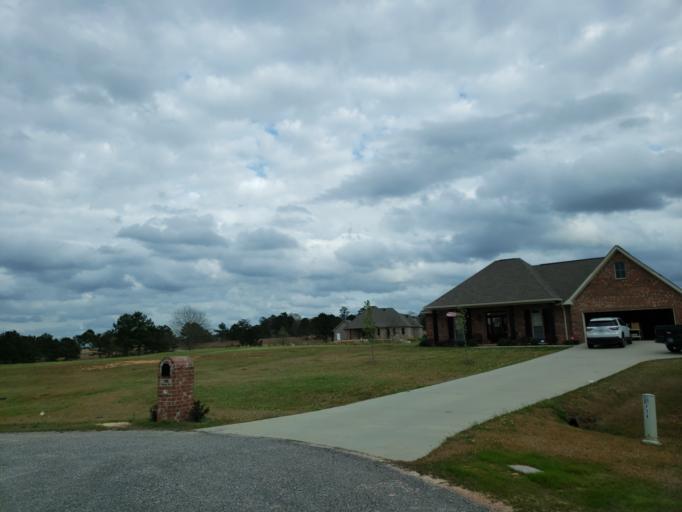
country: US
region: Mississippi
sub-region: Jones County
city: Ellisville
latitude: 31.5533
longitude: -89.2568
